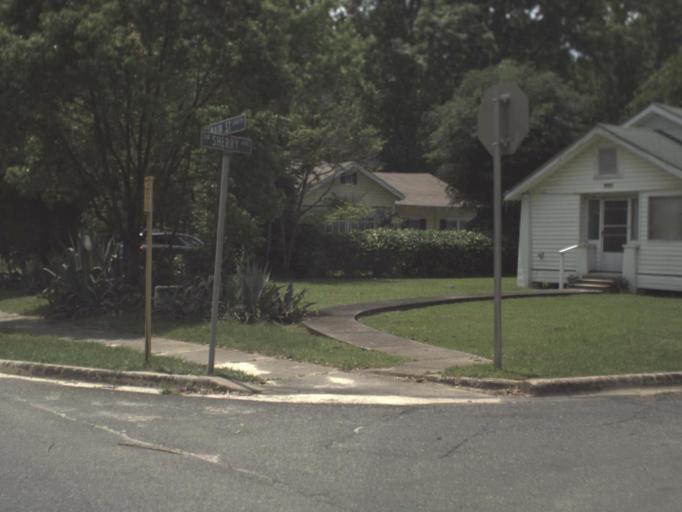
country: US
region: Florida
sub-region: Calhoun County
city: Blountstown
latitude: 30.4399
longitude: -85.0459
